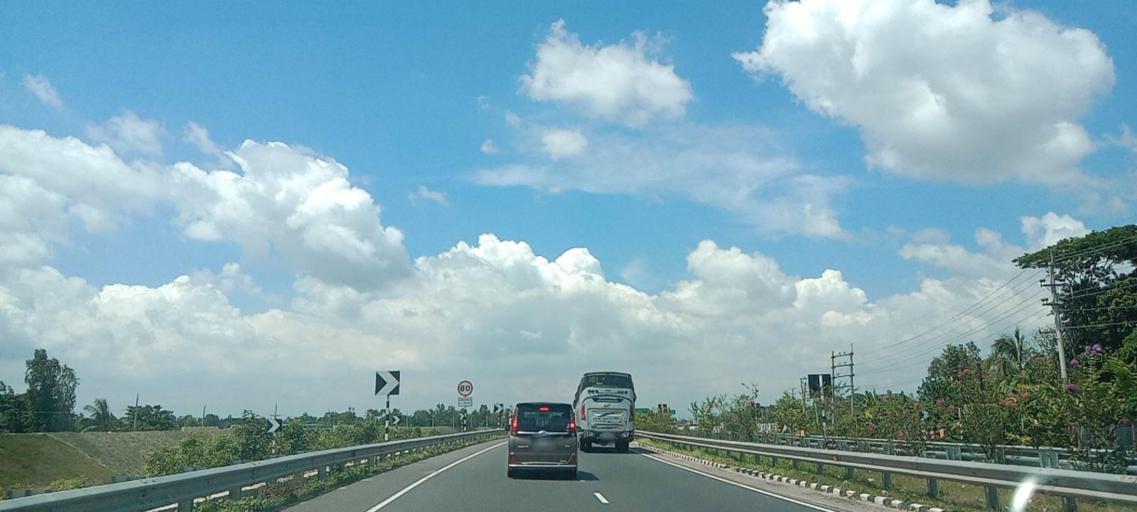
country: BD
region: Dhaka
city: Dohar
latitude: 23.5790
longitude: 90.3052
